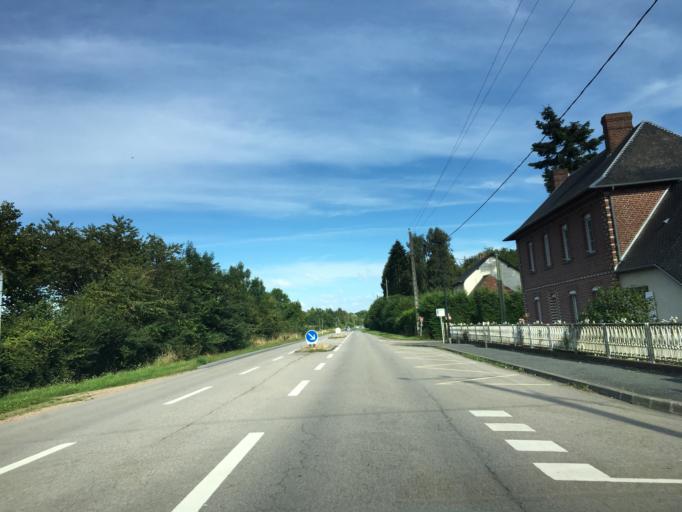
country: FR
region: Lower Normandy
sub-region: Departement du Calvados
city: Cambremer
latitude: 49.1373
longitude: 0.1154
